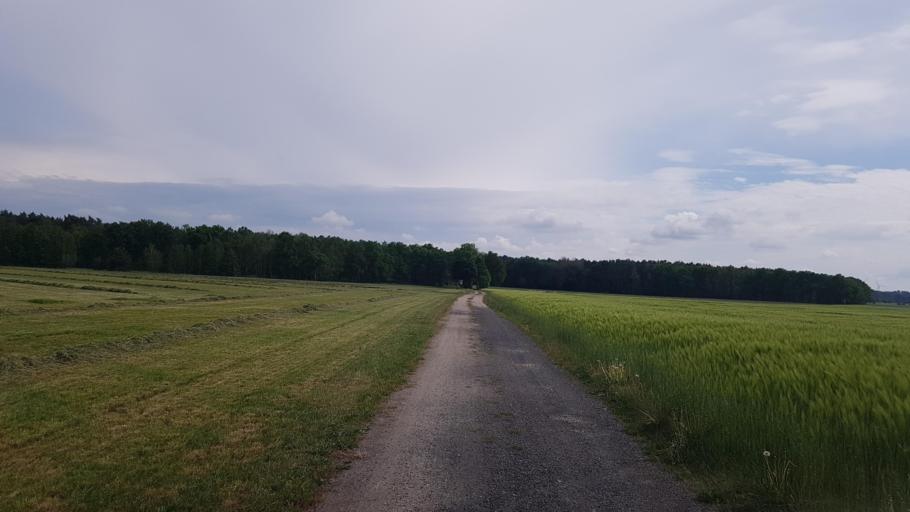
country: DE
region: Brandenburg
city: Sallgast
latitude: 51.6001
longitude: 13.8659
